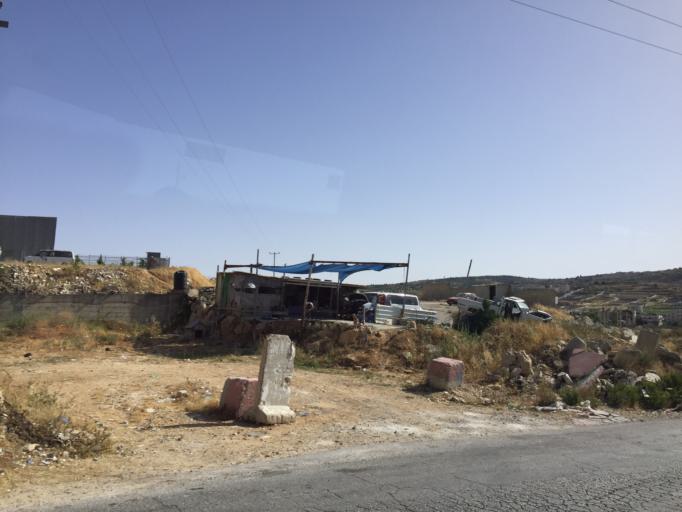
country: PS
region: West Bank
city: Al Khadir
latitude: 31.7043
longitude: 35.1694
